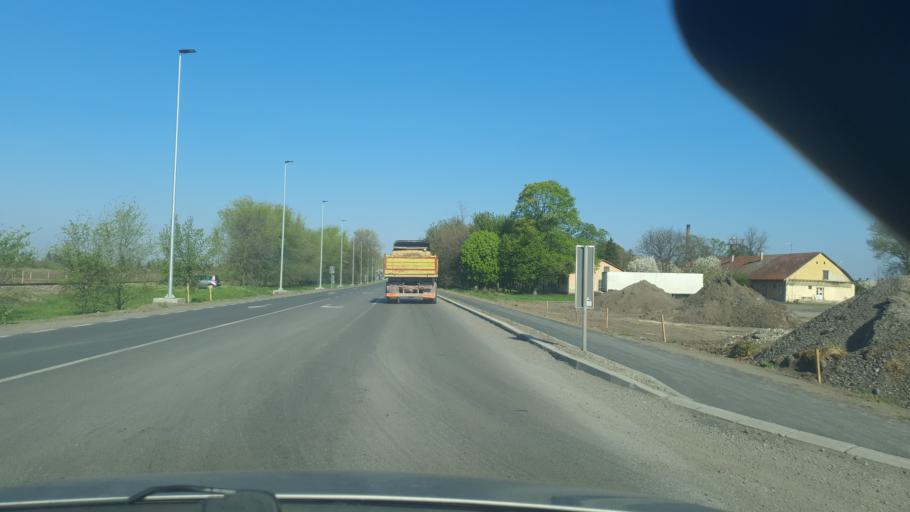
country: RS
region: Autonomna Pokrajina Vojvodina
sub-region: Juznobacki Okrug
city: Vrbas
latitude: 45.5861
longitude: 19.6066
